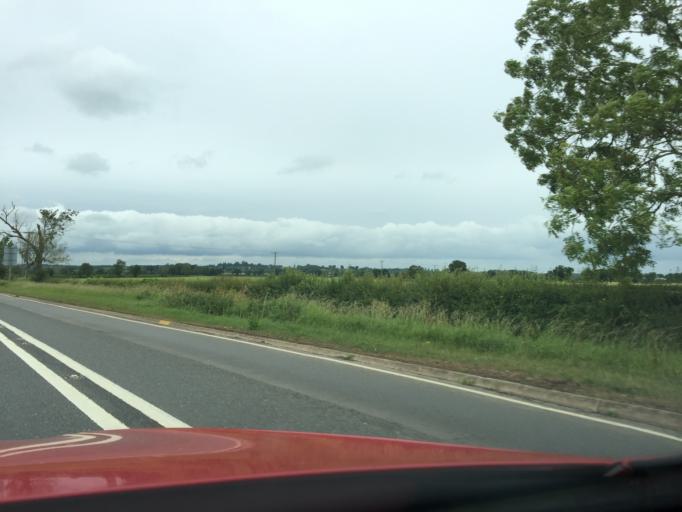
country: GB
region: England
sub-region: Warwickshire
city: Southam
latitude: 52.2536
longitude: -1.3396
